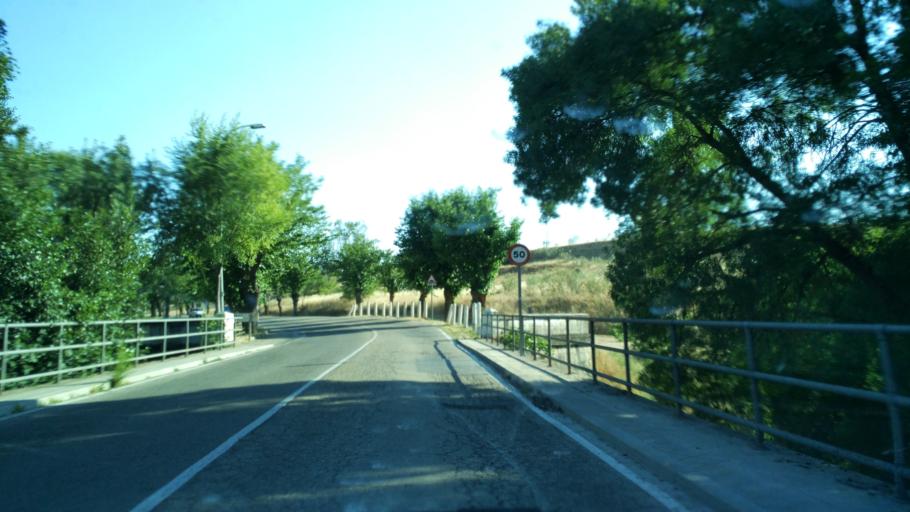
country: ES
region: Madrid
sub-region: Provincia de Madrid
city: San Agustin de Guadalix
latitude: 40.6905
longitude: -3.6097
